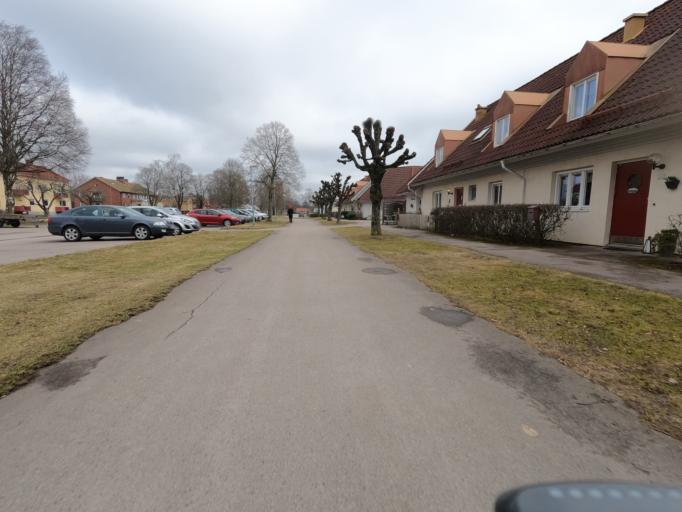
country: SE
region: Kronoberg
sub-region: Ljungby Kommun
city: Ljungby
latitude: 56.8335
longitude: 13.9484
